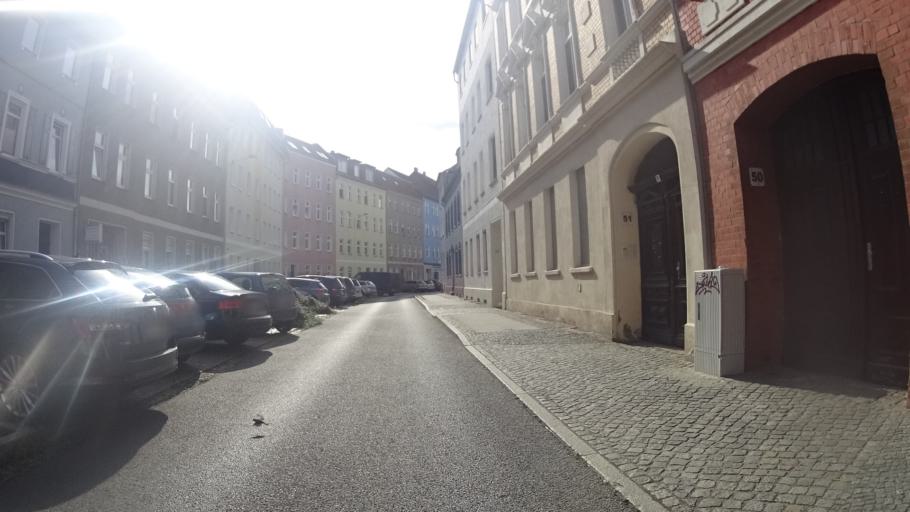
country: DE
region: Brandenburg
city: Brandenburg an der Havel
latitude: 52.4128
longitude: 12.5420
